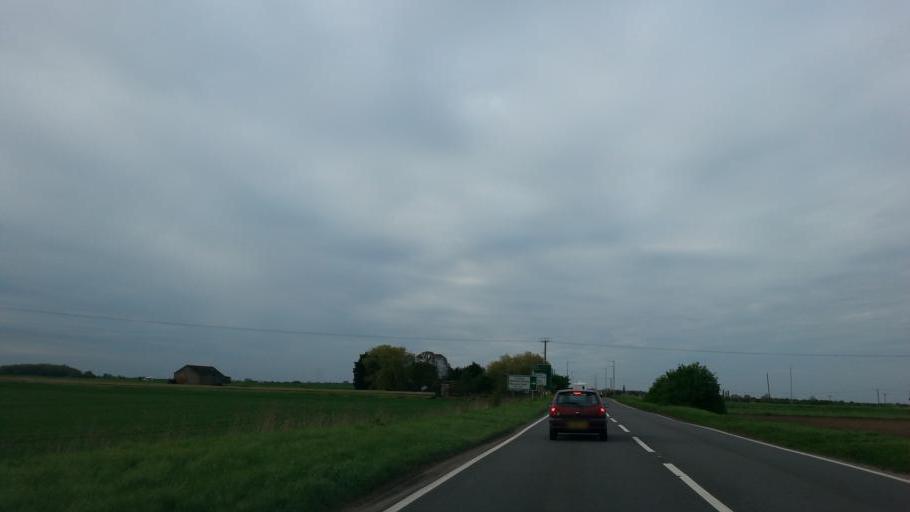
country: GB
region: England
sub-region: Cambridgeshire
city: March
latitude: 52.5881
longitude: 0.0590
